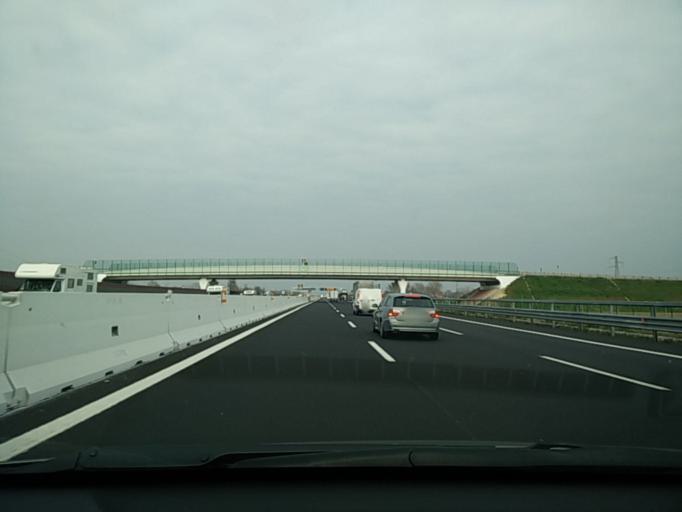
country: IT
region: Veneto
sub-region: Provincia di Treviso
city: Musestre
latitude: 45.6006
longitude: 12.3859
